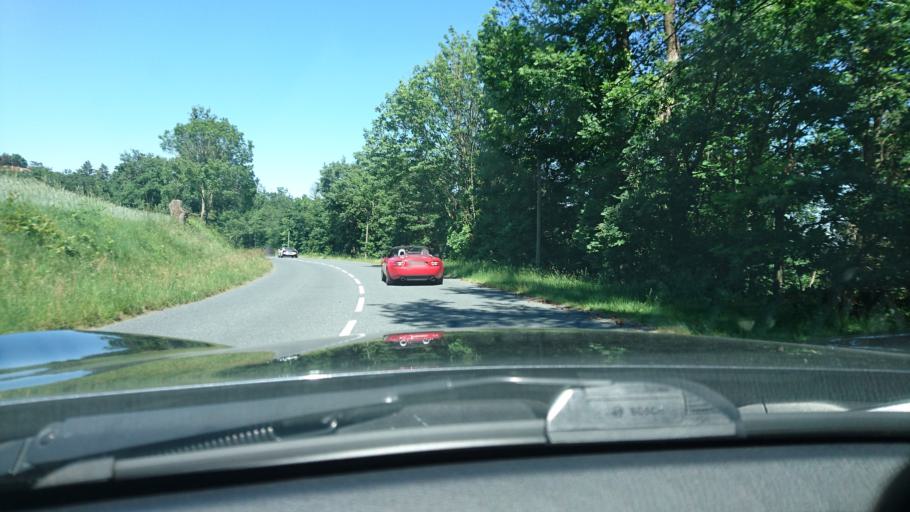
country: FR
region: Rhone-Alpes
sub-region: Departement du Rhone
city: Vaugneray
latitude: 45.7245
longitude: 4.6458
